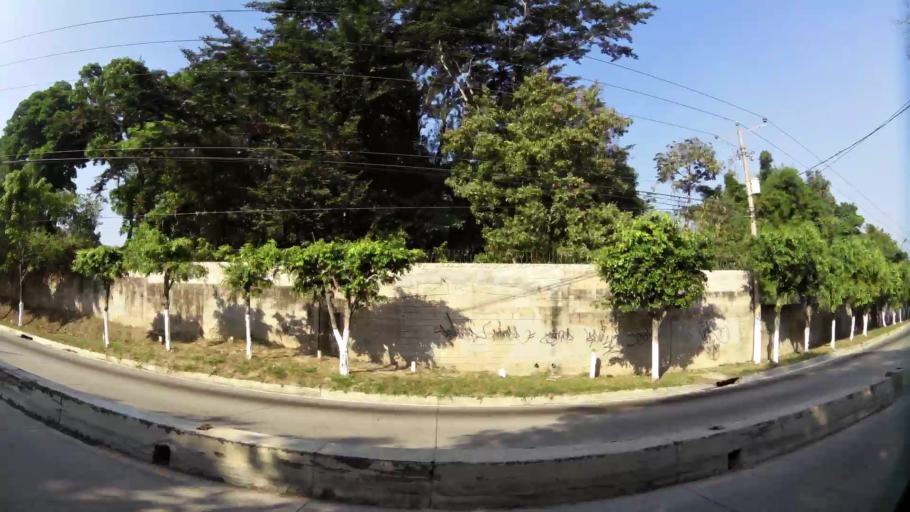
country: SV
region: San Salvador
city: San Salvador
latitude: 13.6747
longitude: -89.2188
